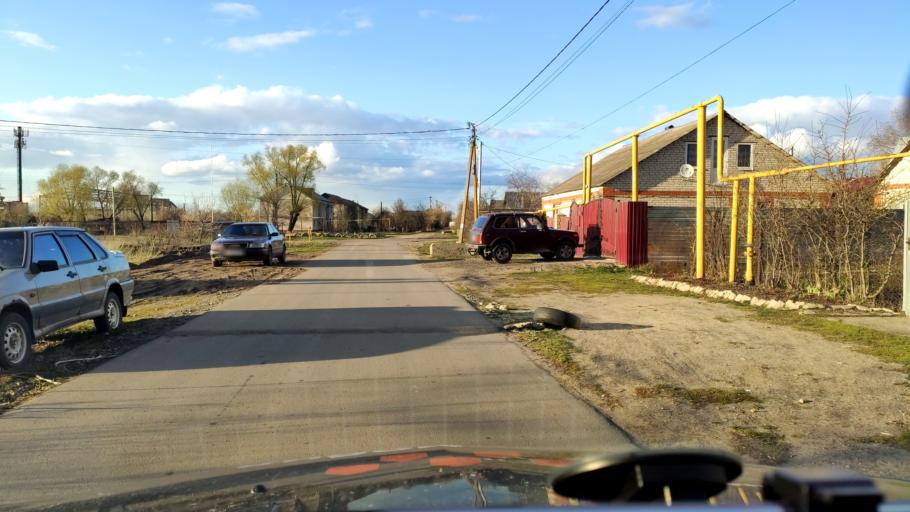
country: RU
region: Voronezj
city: Podgornoye
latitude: 51.8896
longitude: 39.1737
